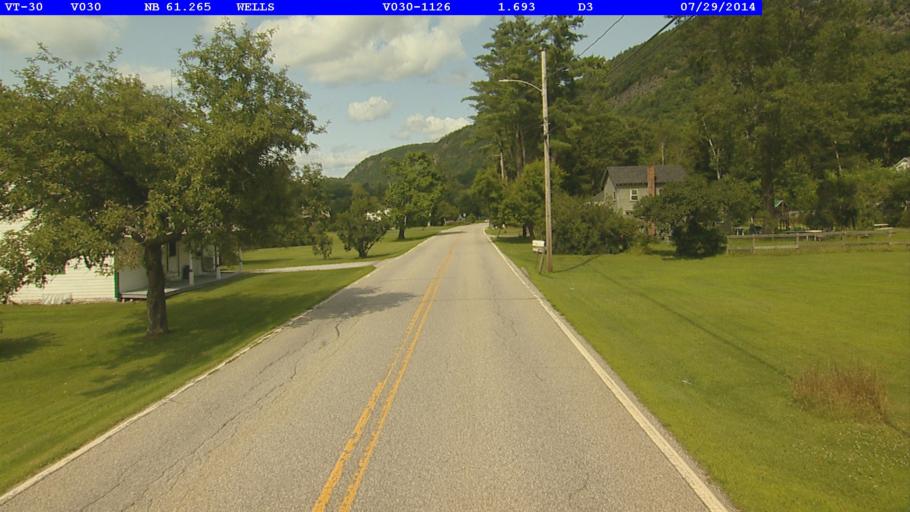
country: US
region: New York
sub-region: Washington County
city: Granville
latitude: 43.4196
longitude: -73.2013
